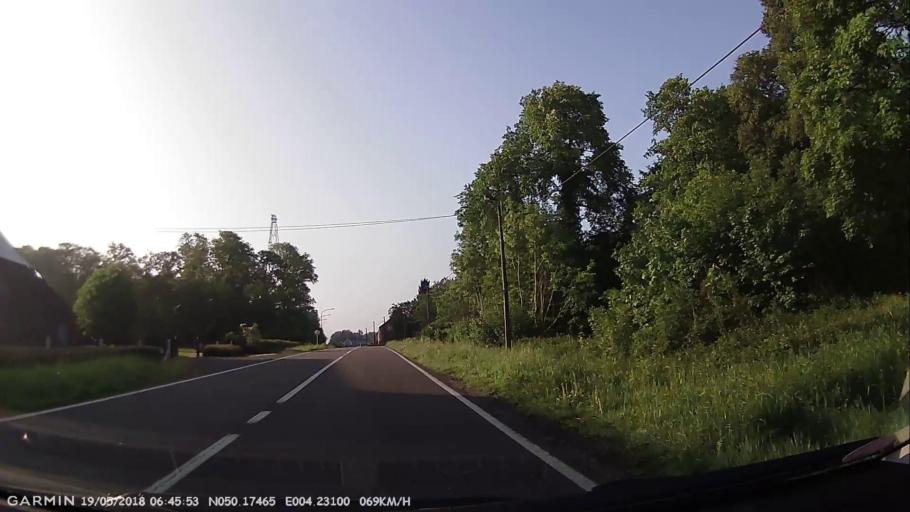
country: BE
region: Wallonia
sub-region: Province du Hainaut
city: Beaumont
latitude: 50.1746
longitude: 4.2311
